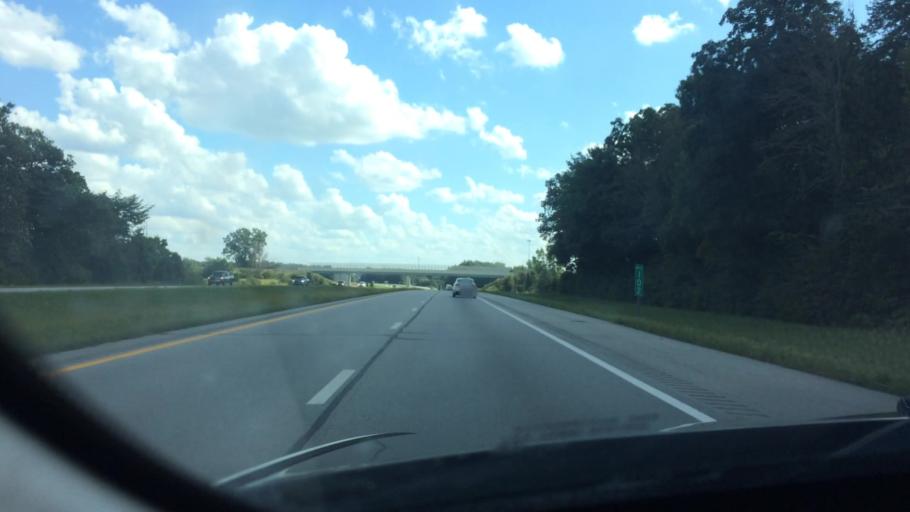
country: US
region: Ohio
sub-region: Shelby County
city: Anna
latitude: 40.4271
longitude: -84.1695
